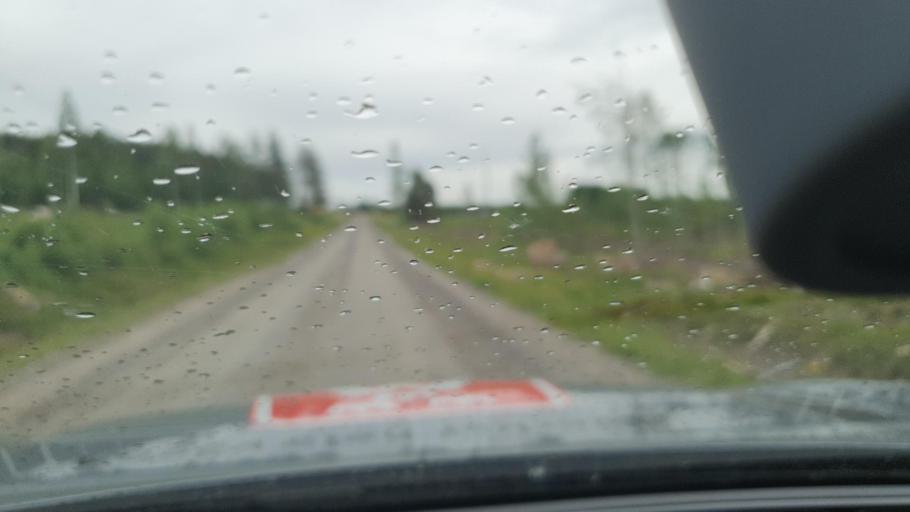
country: SE
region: Norrbotten
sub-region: Kalix Kommun
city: Rolfs
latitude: 66.0460
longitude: 23.0378
